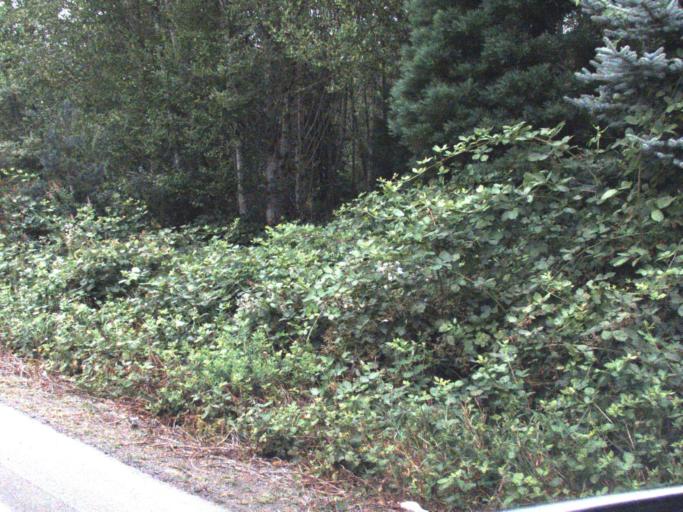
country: US
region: Washington
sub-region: King County
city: Fall City
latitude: 47.5739
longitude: -121.8889
